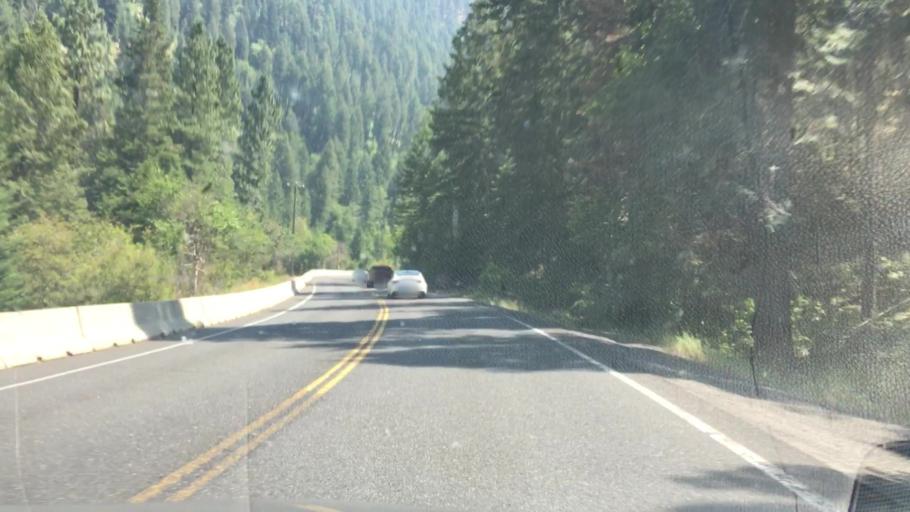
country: US
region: Idaho
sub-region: Valley County
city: McCall
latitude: 45.1385
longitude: -116.2857
